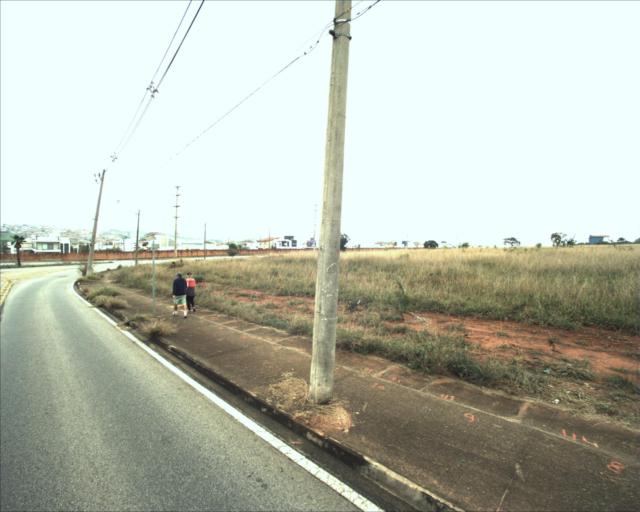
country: BR
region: Sao Paulo
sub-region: Sorocaba
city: Sorocaba
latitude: -23.4520
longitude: -47.4570
